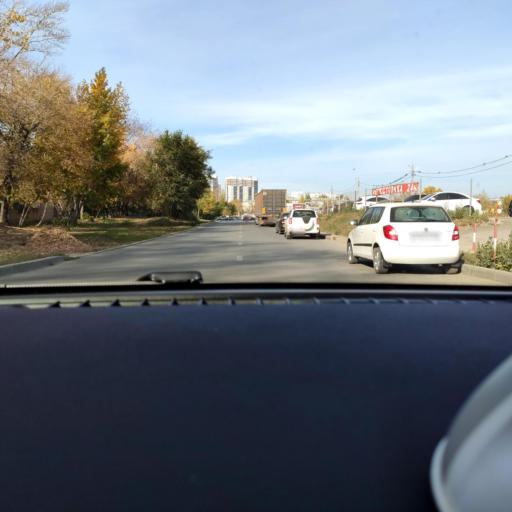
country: RU
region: Samara
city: Samara
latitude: 53.2084
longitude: 50.1939
